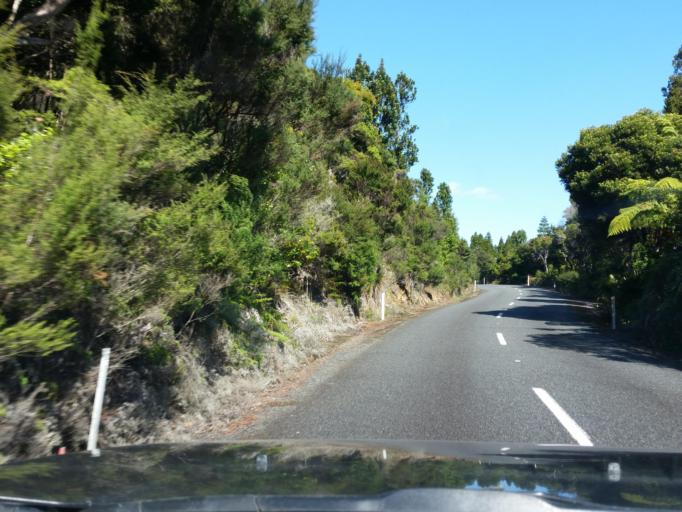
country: NZ
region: Northland
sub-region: Kaipara District
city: Dargaville
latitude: -35.6703
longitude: 173.5747
